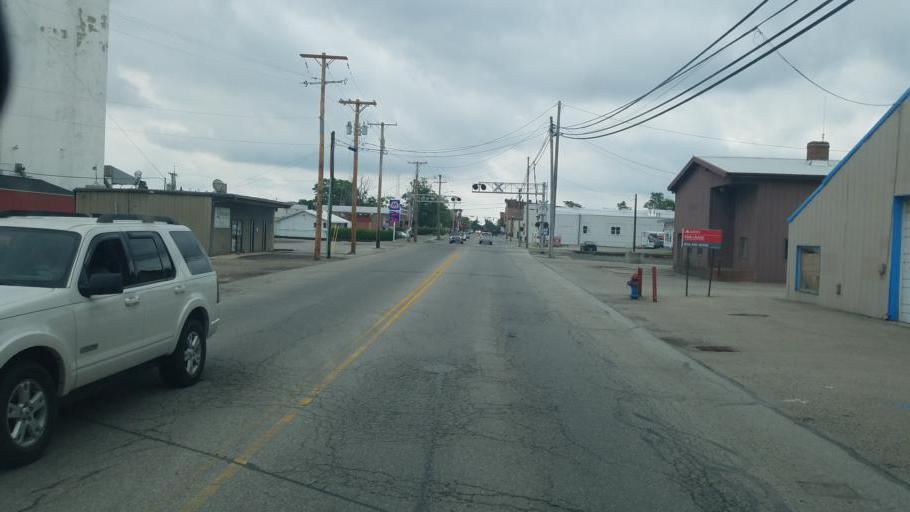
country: US
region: Ohio
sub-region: Union County
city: Marysville
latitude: 40.2398
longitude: -83.3666
